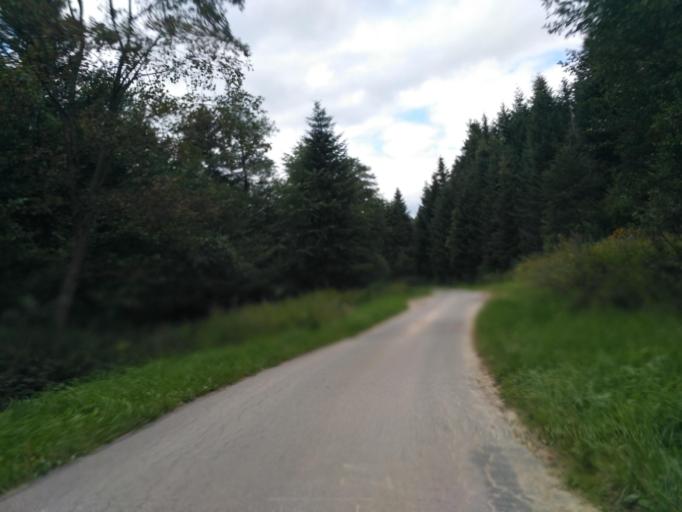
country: PL
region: Subcarpathian Voivodeship
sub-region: Powiat rzeszowski
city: Dynow
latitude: 49.7458
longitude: 22.3053
